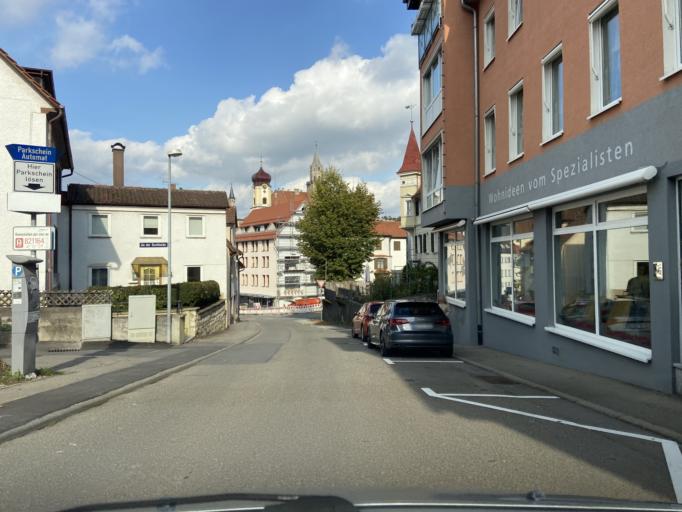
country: DE
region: Baden-Wuerttemberg
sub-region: Tuebingen Region
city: Sigmaringen
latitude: 48.0852
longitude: 9.2155
